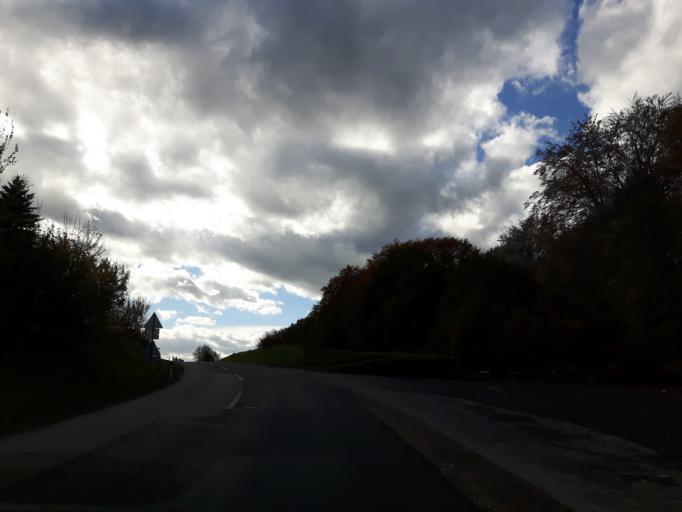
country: AT
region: Styria
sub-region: Politischer Bezirk Suedoststeiermark
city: Baumgarten bei Gnas
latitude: 46.9329
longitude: 15.7489
